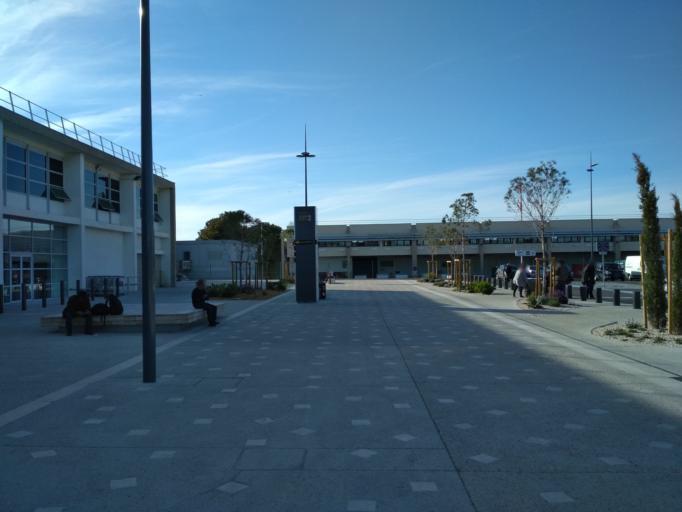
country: FR
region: Provence-Alpes-Cote d'Azur
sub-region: Departement des Bouches-du-Rhone
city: Marignane
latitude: 43.4435
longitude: 5.2195
